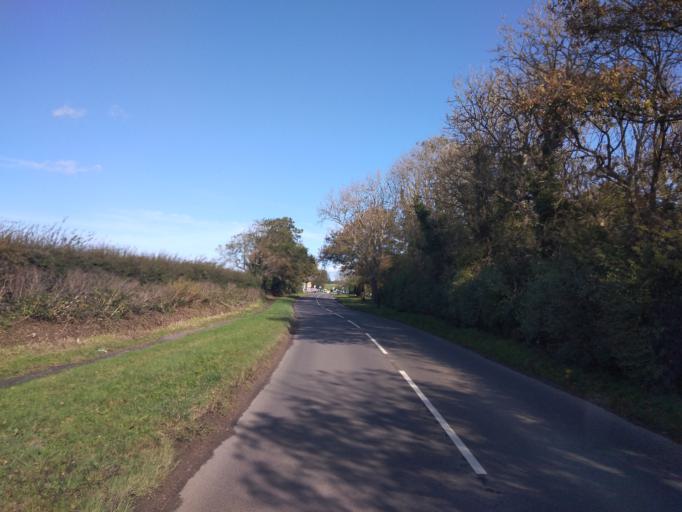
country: GB
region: England
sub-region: East Sussex
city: Seaford
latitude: 50.8244
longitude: 0.1626
